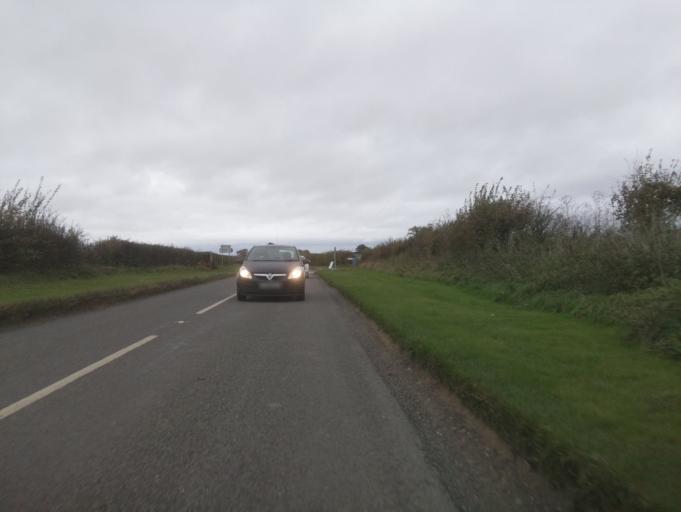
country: GB
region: England
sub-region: Dorset
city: Sherborne
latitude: 50.9743
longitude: -2.5579
